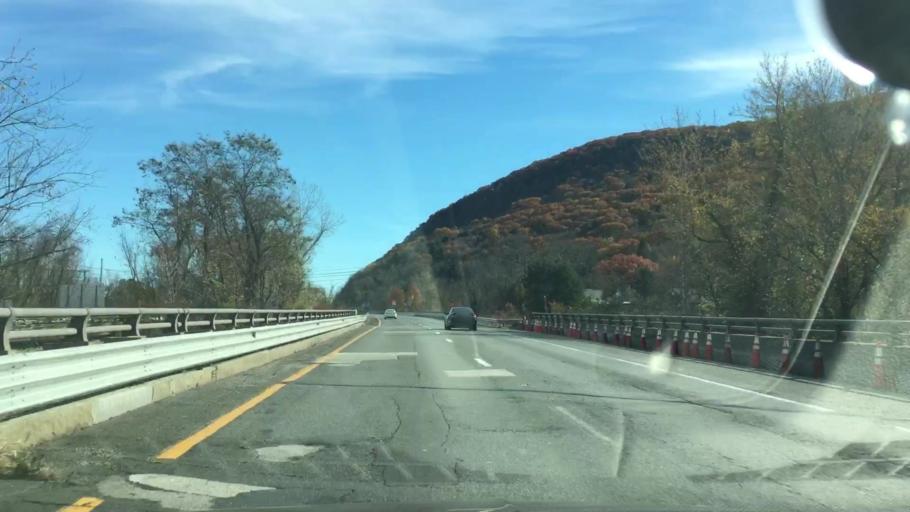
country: US
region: Massachusetts
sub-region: Hampshire County
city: Northampton
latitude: 42.2880
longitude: -72.6235
